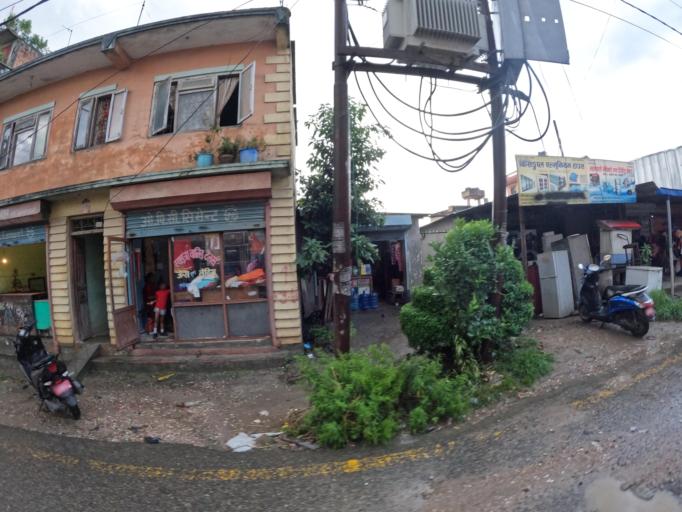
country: NP
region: Central Region
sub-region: Bagmati Zone
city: Kathmandu
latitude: 27.7624
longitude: 85.3305
